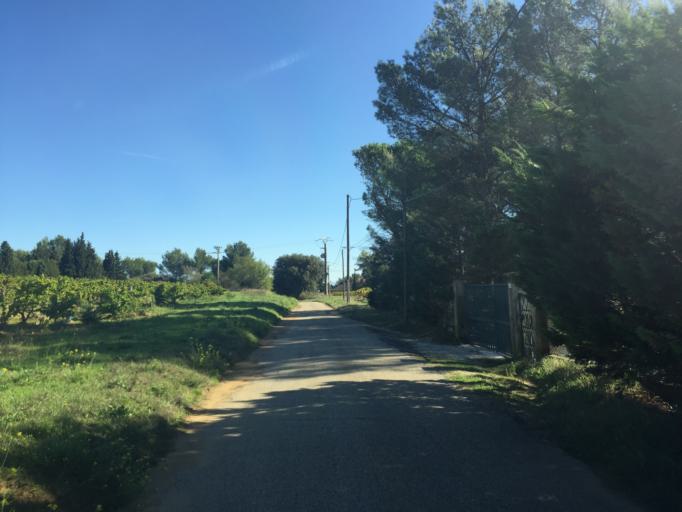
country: FR
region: Provence-Alpes-Cote d'Azur
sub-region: Departement du Vaucluse
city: Courthezon
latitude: 44.0820
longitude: 4.8548
